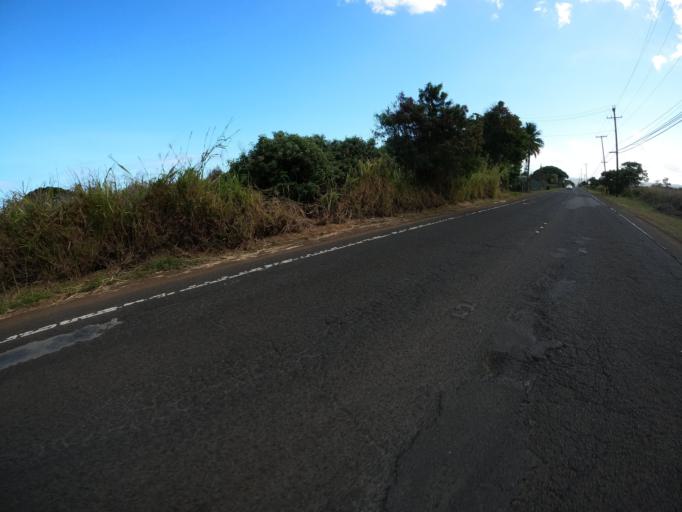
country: US
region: Hawaii
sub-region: Honolulu County
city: Mokuleia
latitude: 21.5757
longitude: -158.1613
